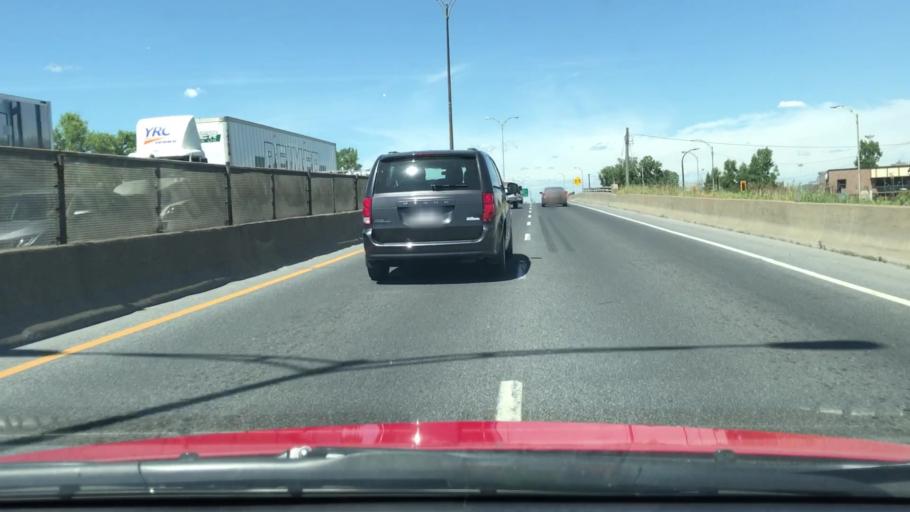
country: CA
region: Quebec
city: Montreal-Ouest
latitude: 45.4330
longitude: -73.6504
